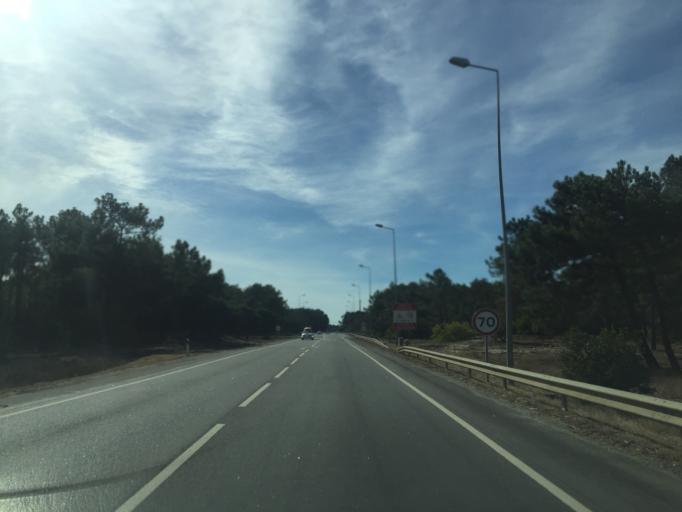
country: PT
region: Coimbra
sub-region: Figueira da Foz
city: Lavos
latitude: 40.0942
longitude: -8.8545
